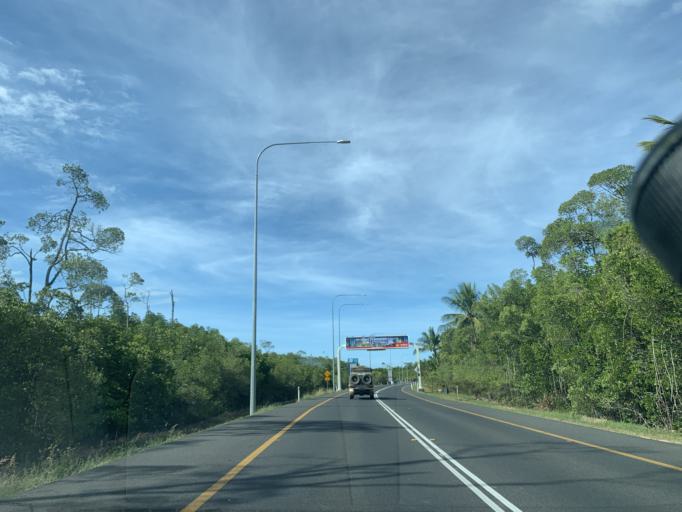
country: AU
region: Queensland
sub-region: Cairns
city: Cairns
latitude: -16.8911
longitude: 145.7609
